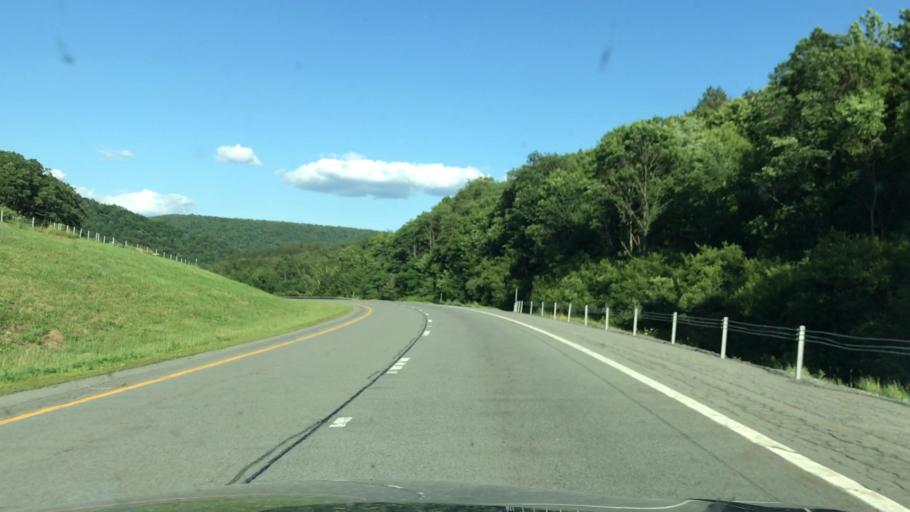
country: US
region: New York
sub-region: Sullivan County
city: Livingston Manor
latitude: 41.9513
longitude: -74.9796
